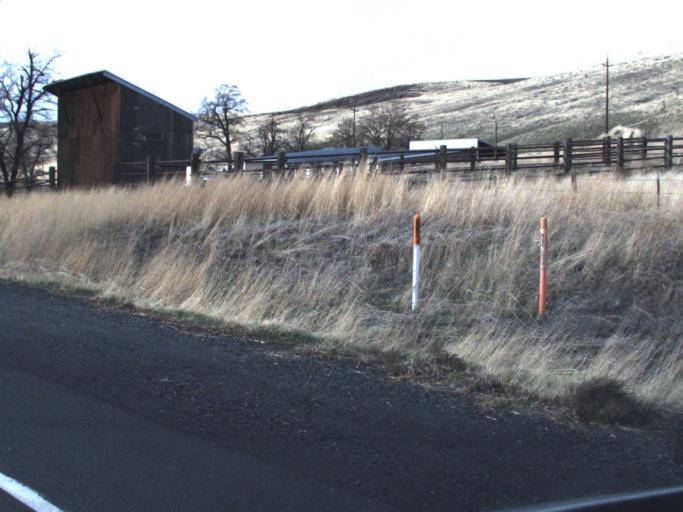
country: US
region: Washington
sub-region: Garfield County
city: Pomeroy
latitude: 46.4748
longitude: -117.5619
